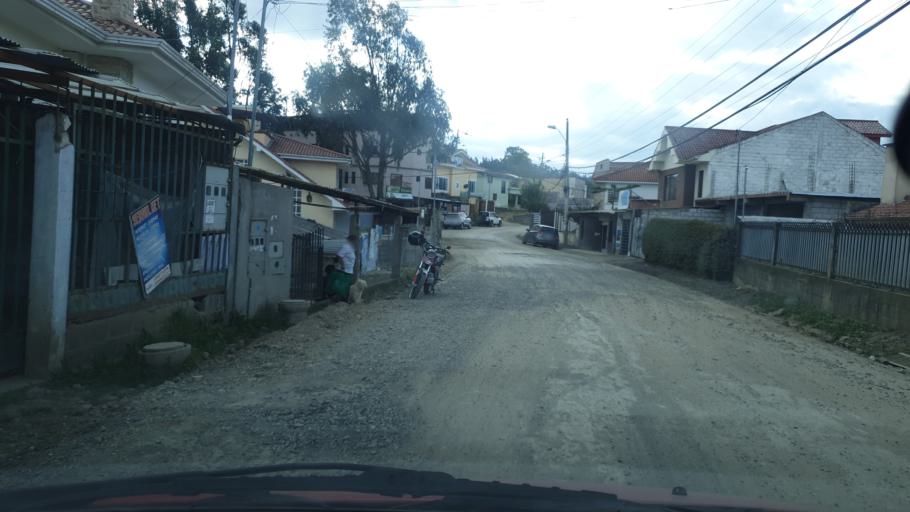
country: EC
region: Azuay
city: Cuenca
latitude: -2.9247
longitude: -78.9733
